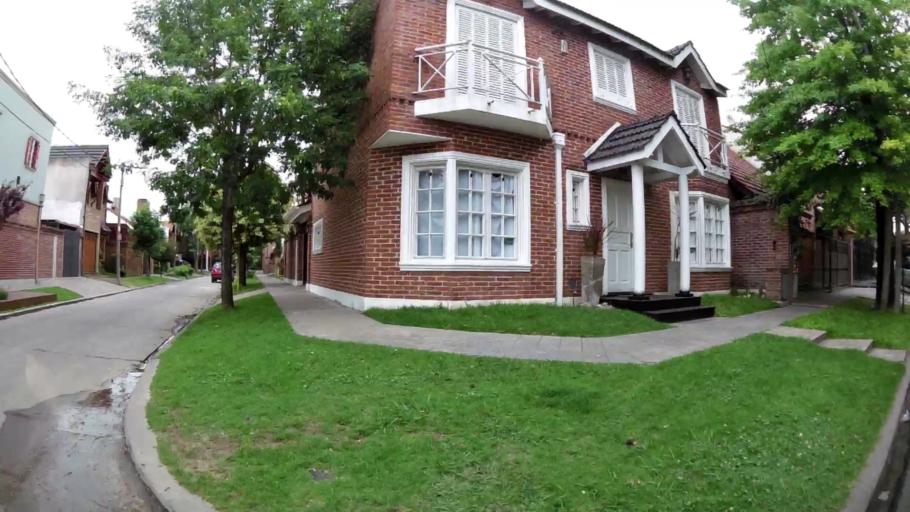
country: AR
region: Buenos Aires F.D.
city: Villa Lugano
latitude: -34.7229
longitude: -58.5176
